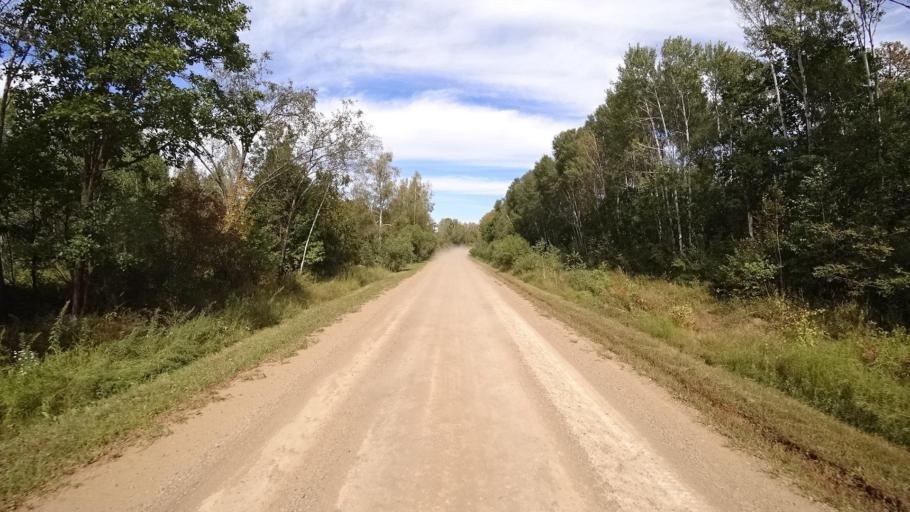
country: RU
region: Primorskiy
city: Yakovlevka
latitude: 44.6931
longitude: 133.6190
